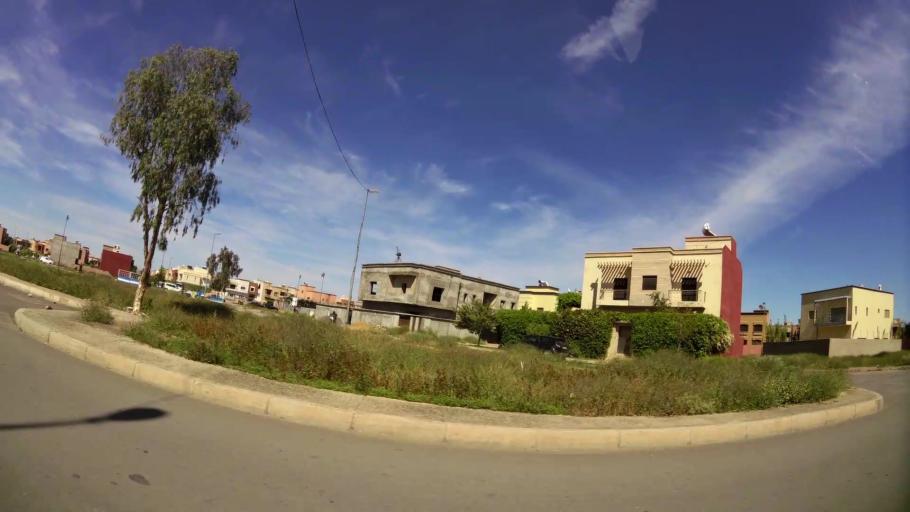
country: MA
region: Marrakech-Tensift-Al Haouz
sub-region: Marrakech
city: Marrakesh
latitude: 31.6437
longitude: -8.0433
